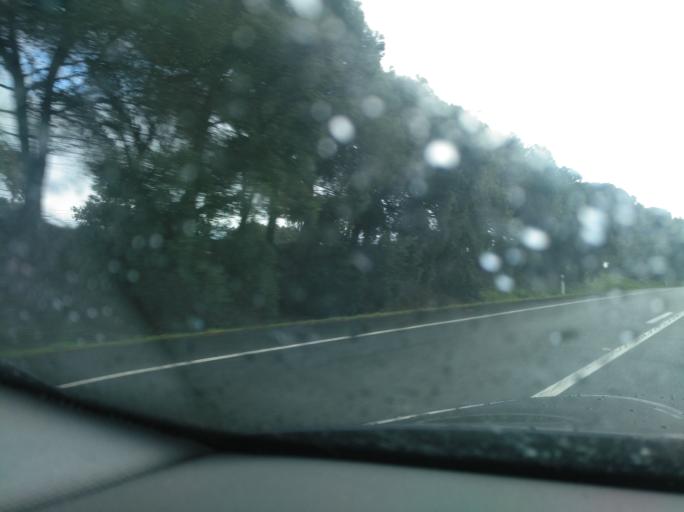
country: PT
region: Setubal
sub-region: Grandola
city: Grandola
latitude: 38.0806
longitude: -8.4171
